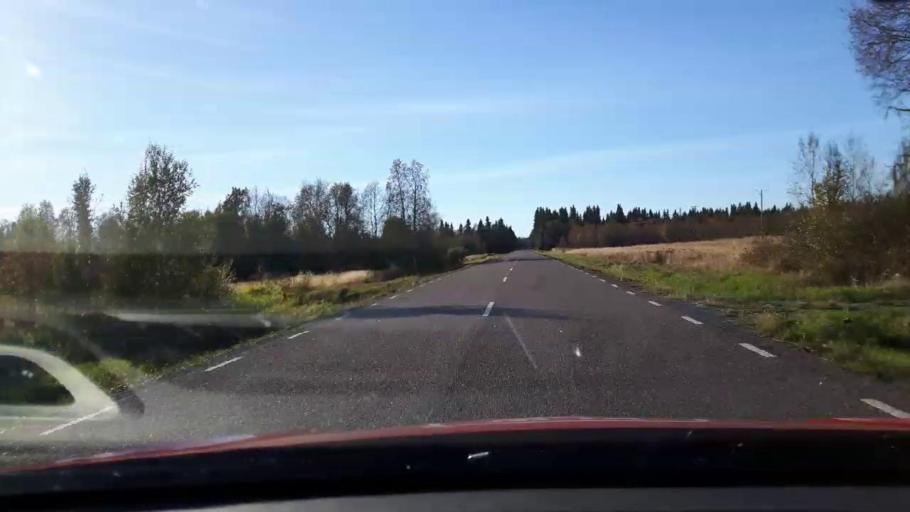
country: SE
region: Jaemtland
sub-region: Stroemsunds Kommun
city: Stroemsund
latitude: 63.8460
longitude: 15.2949
